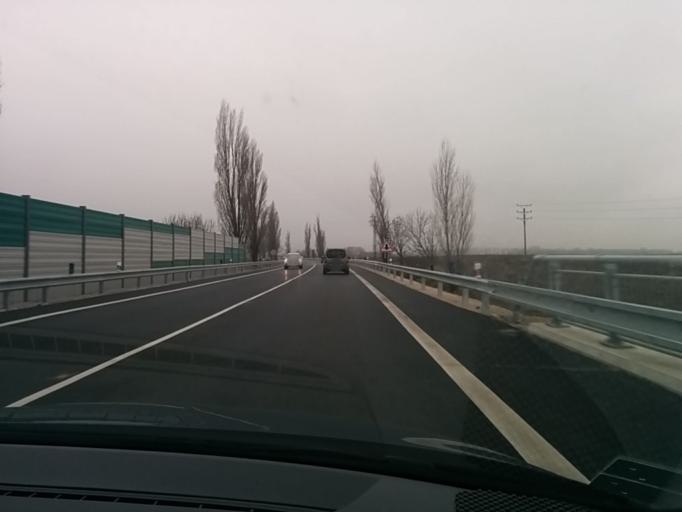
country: SK
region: Trnavsky
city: Sladkovicovo
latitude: 48.2033
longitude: 17.6207
